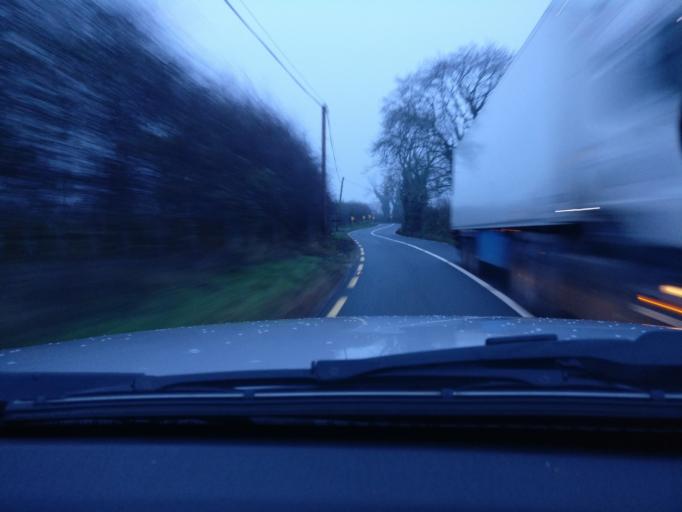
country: IE
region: Leinster
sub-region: An Mhi
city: Athboy
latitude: 53.6073
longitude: -6.9737
